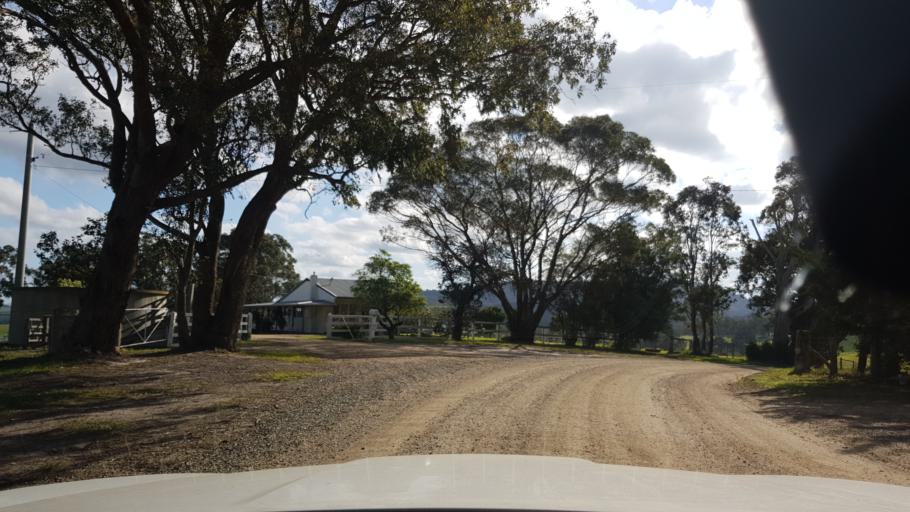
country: AU
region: Victoria
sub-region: East Gippsland
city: Bairnsdale
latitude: -37.7828
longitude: 147.5753
